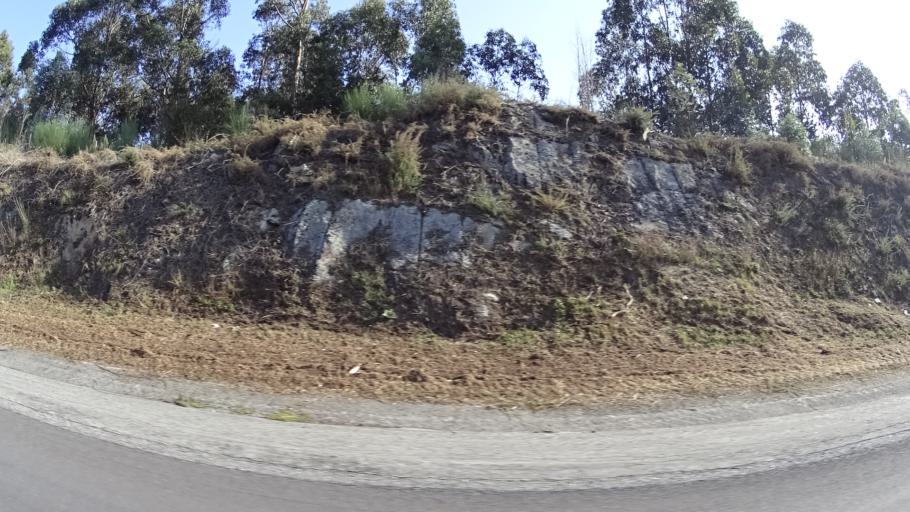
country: ES
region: Galicia
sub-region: Provincia da Coruna
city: Coiros
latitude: 43.2438
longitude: -8.1450
